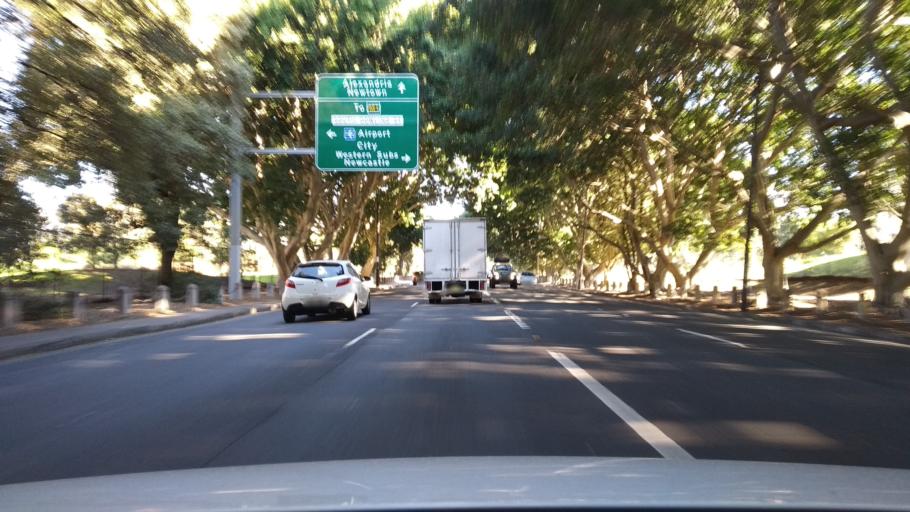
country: AU
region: New South Wales
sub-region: City of Sydney
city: Redfern
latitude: -33.9011
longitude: 151.2177
